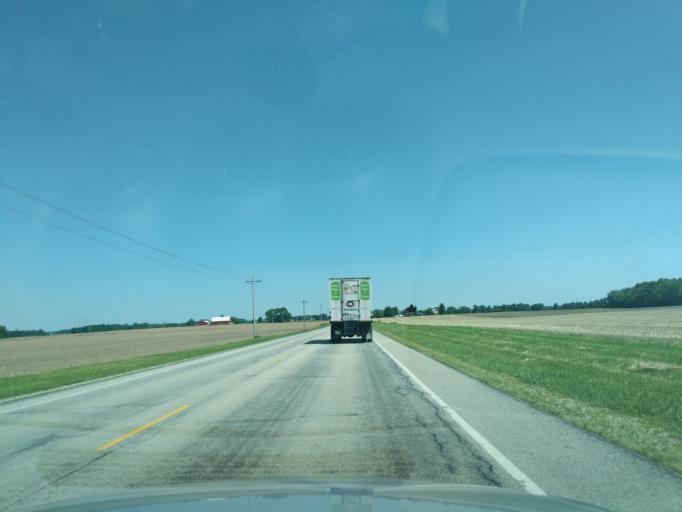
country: US
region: Indiana
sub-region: Huntington County
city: Roanoke
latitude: 41.0361
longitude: -85.4706
